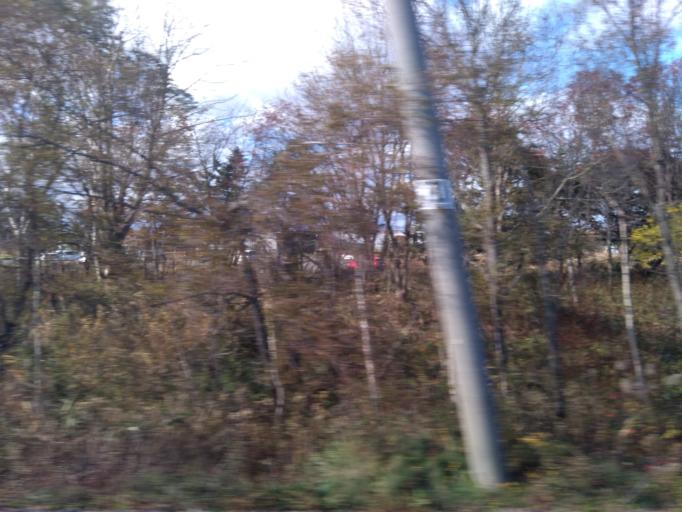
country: JP
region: Hokkaido
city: Shiraoi
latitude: 42.5154
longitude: 141.2963
